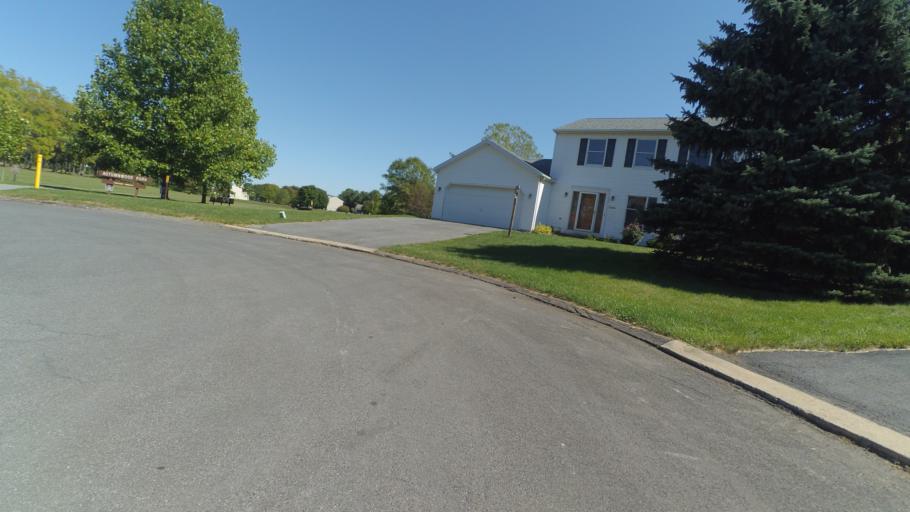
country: US
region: Pennsylvania
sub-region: Centre County
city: Pine Grove Mills
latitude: 40.7635
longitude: -77.8893
